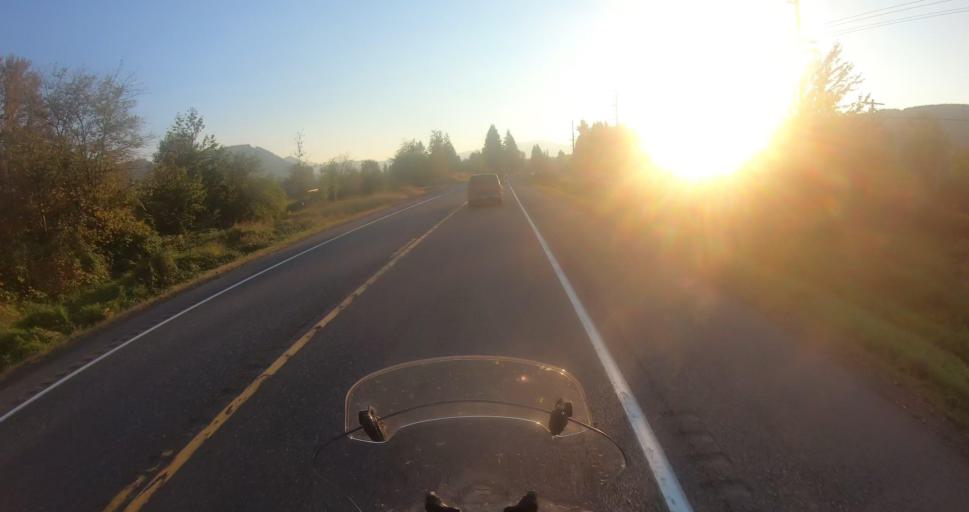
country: US
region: Washington
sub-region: Lewis County
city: Morton
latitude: 46.5210
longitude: -122.1524
